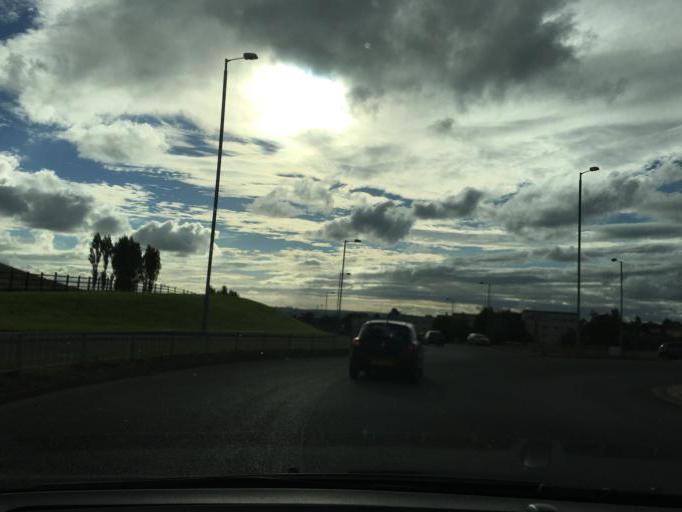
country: GB
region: Scotland
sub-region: North Lanarkshire
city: Holytown
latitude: 55.8007
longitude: -3.9646
